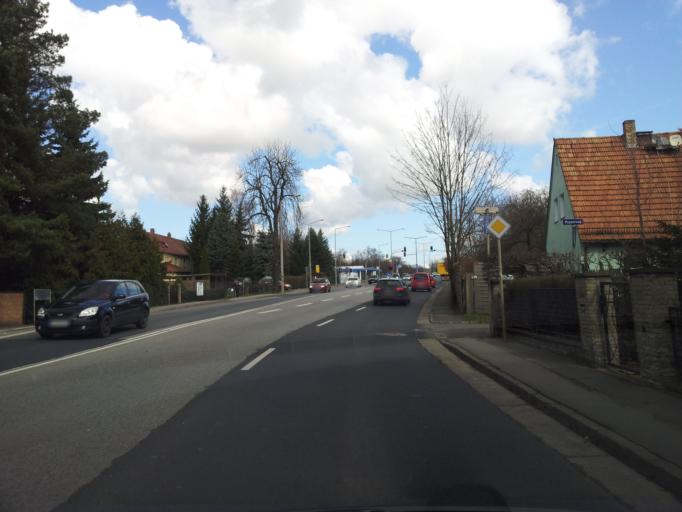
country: DE
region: Saxony
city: Albertstadt
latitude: 51.0922
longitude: 13.7373
